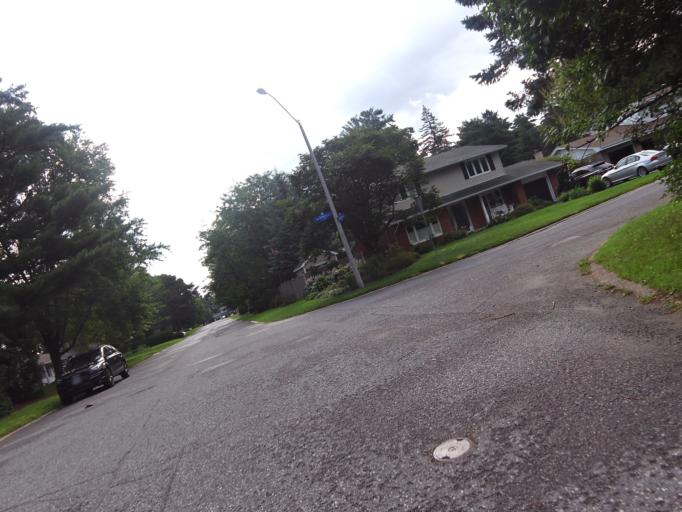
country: CA
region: Ontario
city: Bells Corners
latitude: 45.3244
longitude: -75.7909
